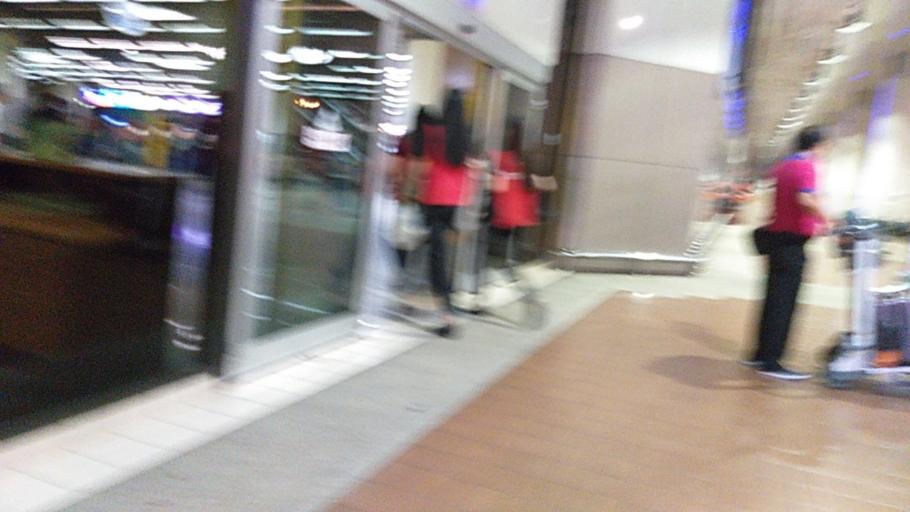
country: TH
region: Bangkok
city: Don Mueang
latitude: 13.9212
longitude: 100.6028
